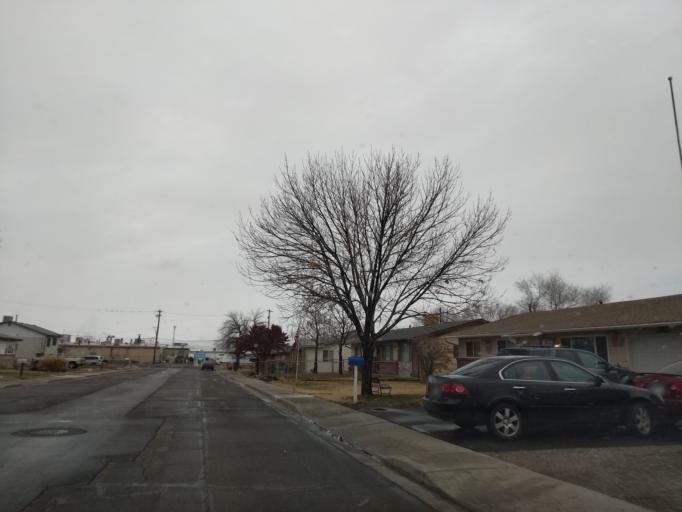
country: US
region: Colorado
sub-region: Mesa County
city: Grand Junction
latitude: 39.0747
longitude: -108.5254
